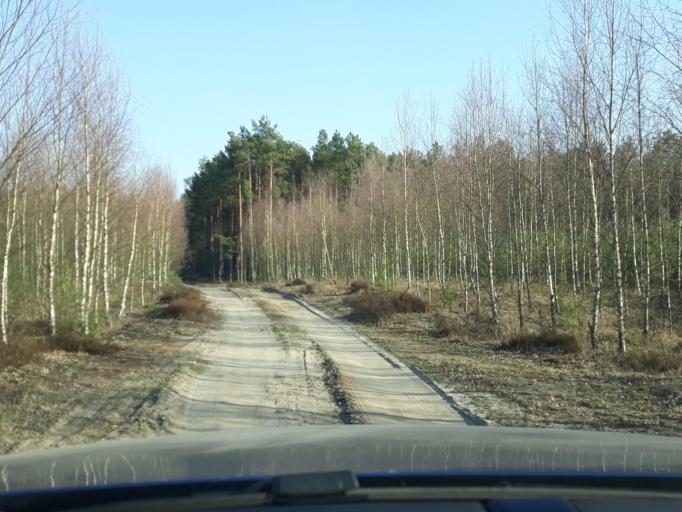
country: PL
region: Pomeranian Voivodeship
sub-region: Powiat bytowski
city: Lipnica
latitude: 53.9162
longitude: 17.4736
